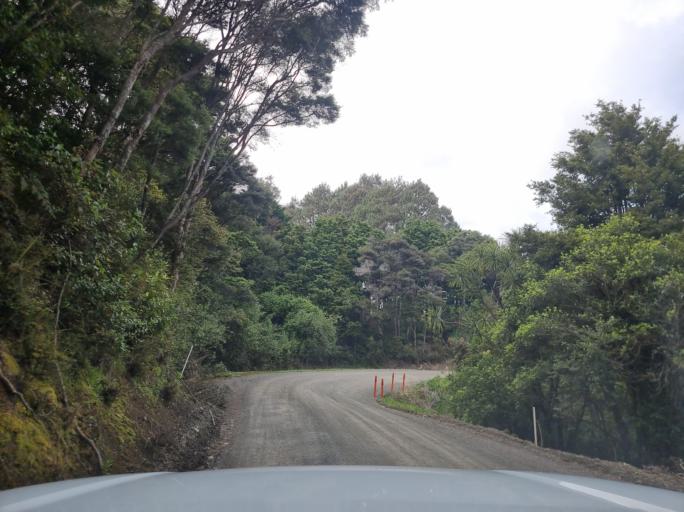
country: NZ
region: Northland
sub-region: Whangarei
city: Ruakaka
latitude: -36.1083
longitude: 174.2101
